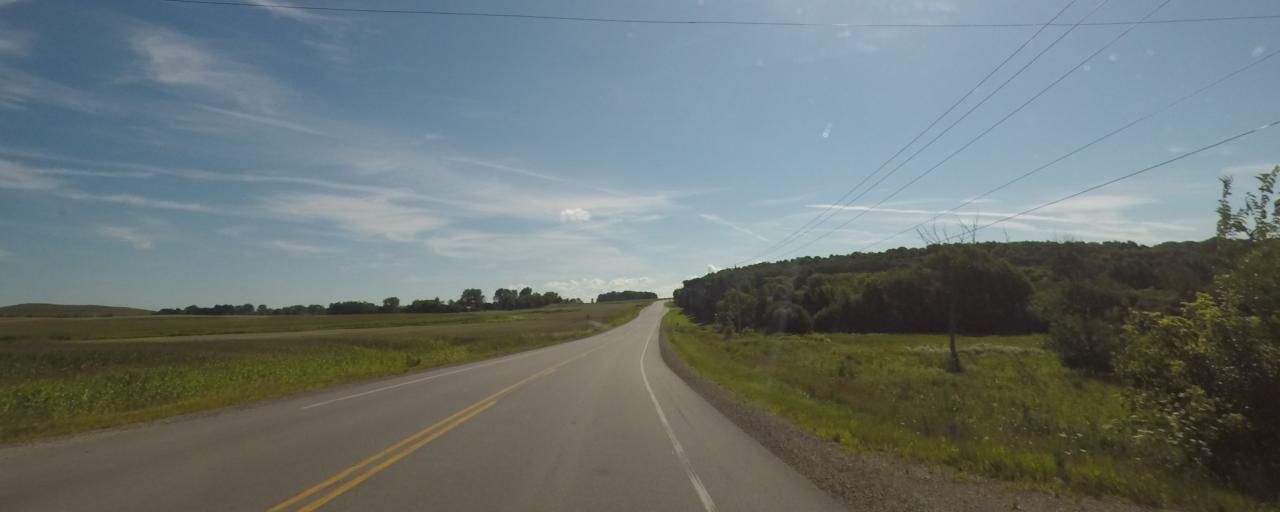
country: US
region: Wisconsin
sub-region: Jefferson County
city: Johnson Creek
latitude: 43.0763
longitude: -88.7569
